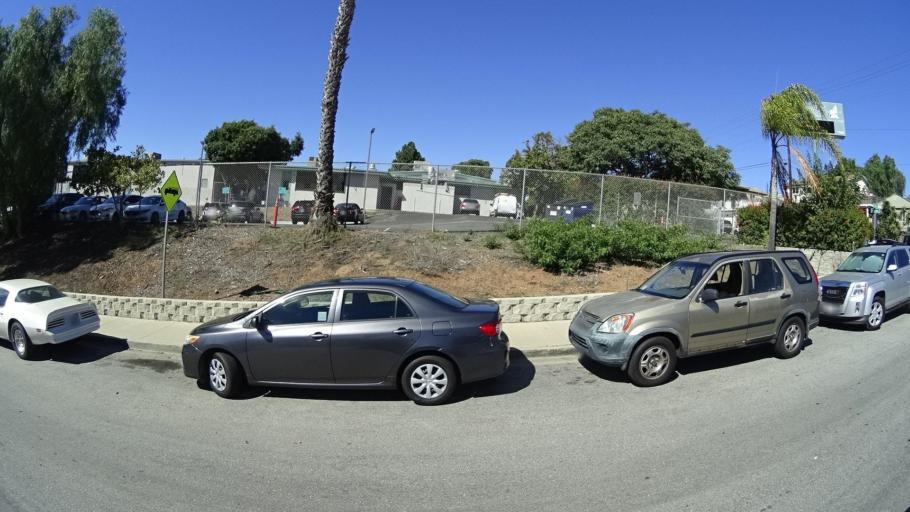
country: US
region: California
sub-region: San Diego County
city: National City
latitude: 32.6694
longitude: -117.0753
